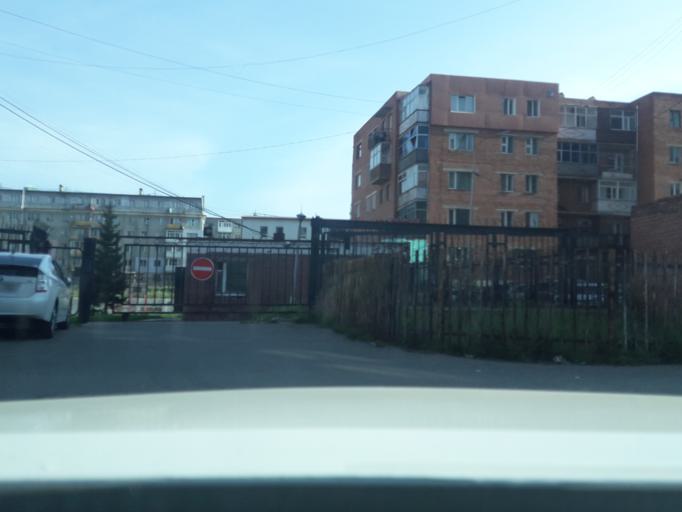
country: MN
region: Ulaanbaatar
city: Ulaanbaatar
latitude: 47.9207
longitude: 106.9461
